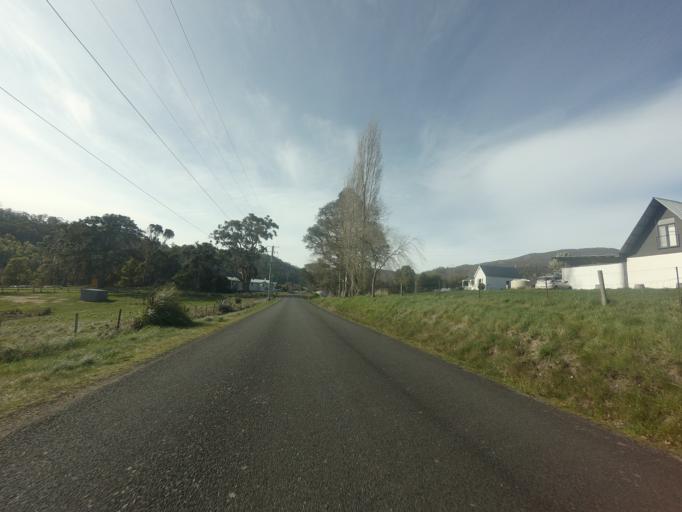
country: AU
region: Tasmania
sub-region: Huon Valley
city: Cygnet
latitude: -43.1811
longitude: 147.1259
